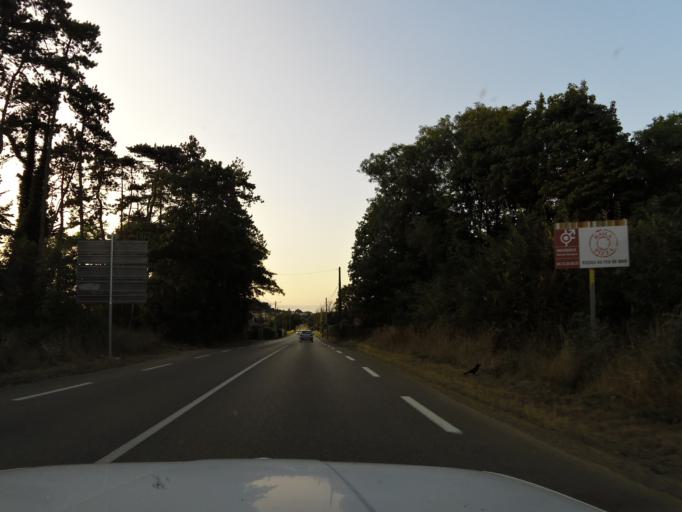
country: FR
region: Rhone-Alpes
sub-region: Departement de l'Ain
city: Meximieux
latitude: 45.8930
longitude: 5.1912
